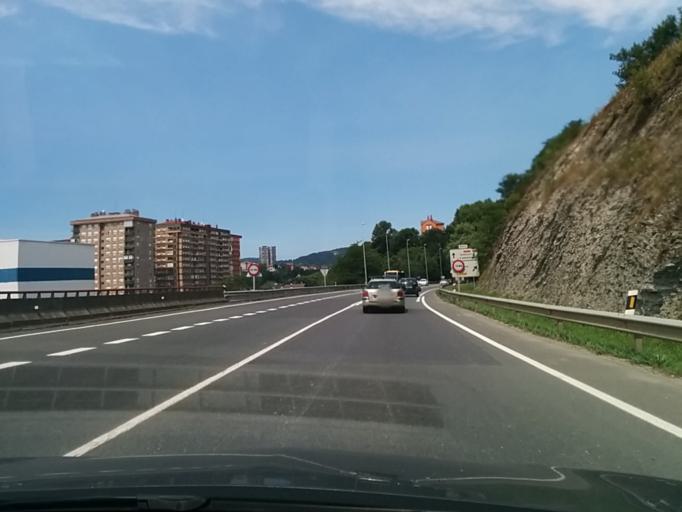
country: ES
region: Basque Country
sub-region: Provincia de Guipuzcoa
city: Lezo
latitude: 43.3146
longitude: -1.8953
